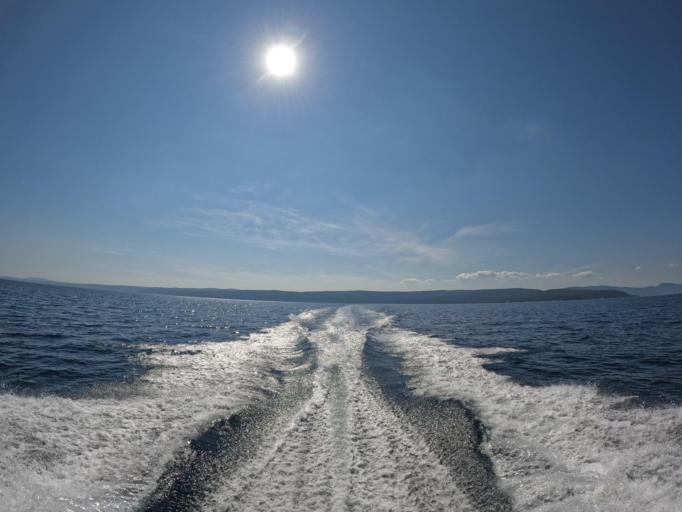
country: HR
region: Primorsko-Goranska
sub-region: Grad Krk
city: Krk
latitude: 44.9473
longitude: 14.5270
